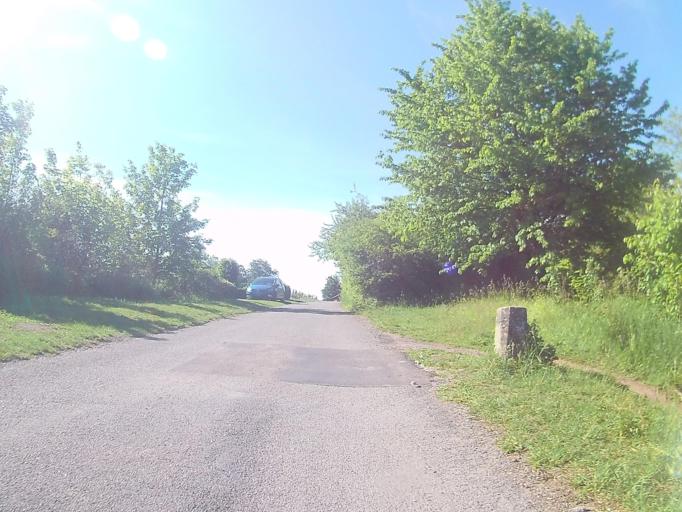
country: DE
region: Baden-Wuerttemberg
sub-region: Regierungsbezirk Stuttgart
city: Fellbach
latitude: 48.7785
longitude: 9.2930
